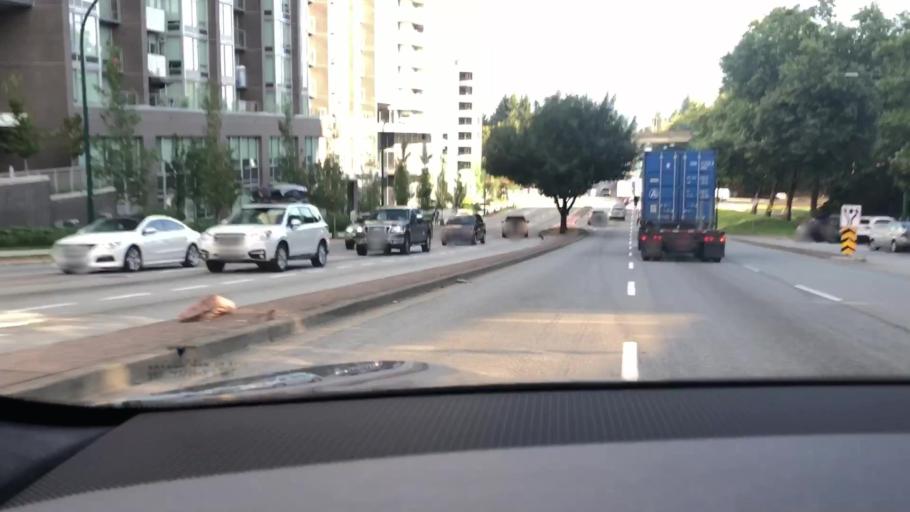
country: CA
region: British Columbia
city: Burnaby
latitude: 49.2328
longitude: -123.0234
